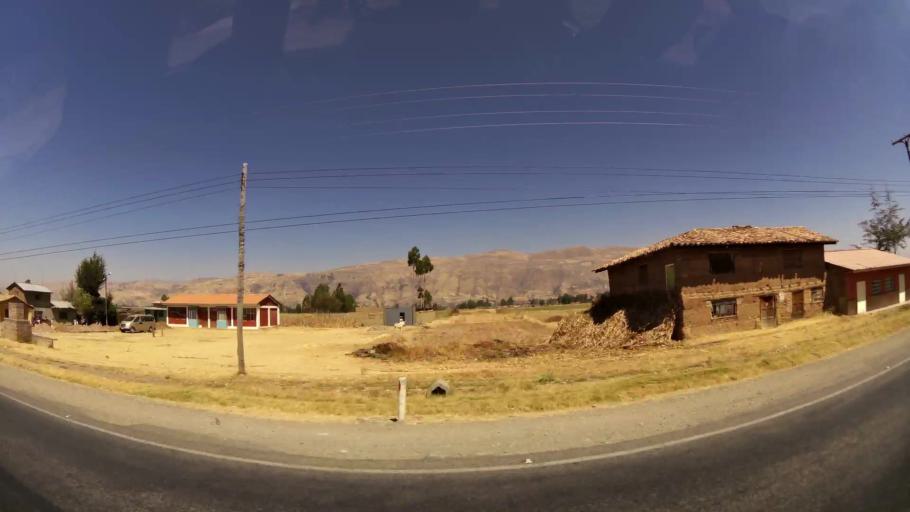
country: PE
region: Junin
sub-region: Provincia de Jauja
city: San Lorenzo
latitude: -11.8404
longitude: -75.3907
